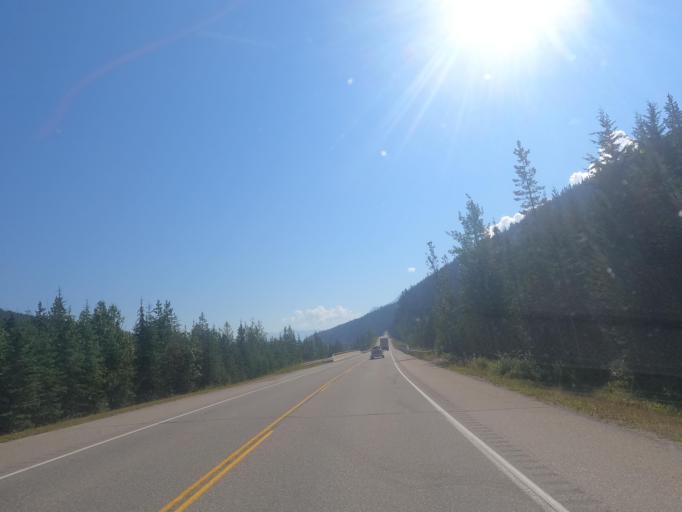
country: CA
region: Alberta
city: Jasper Park Lodge
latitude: 52.8760
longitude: -118.3163
